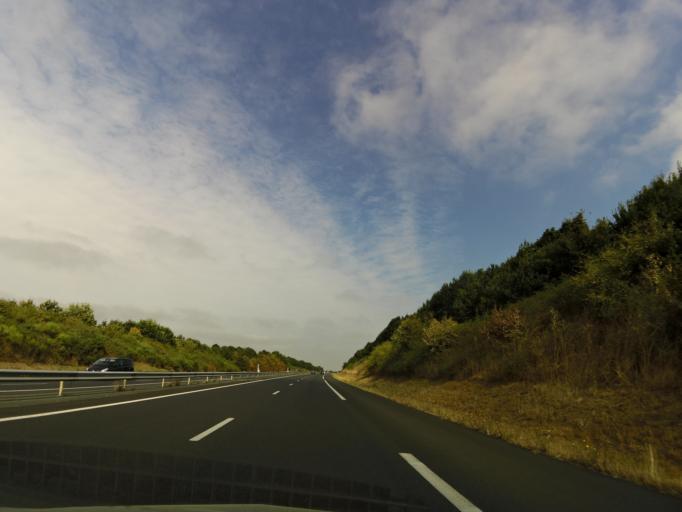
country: FR
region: Pays de la Loire
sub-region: Departement de la Vendee
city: Chauche
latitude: 46.8497
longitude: -1.2716
